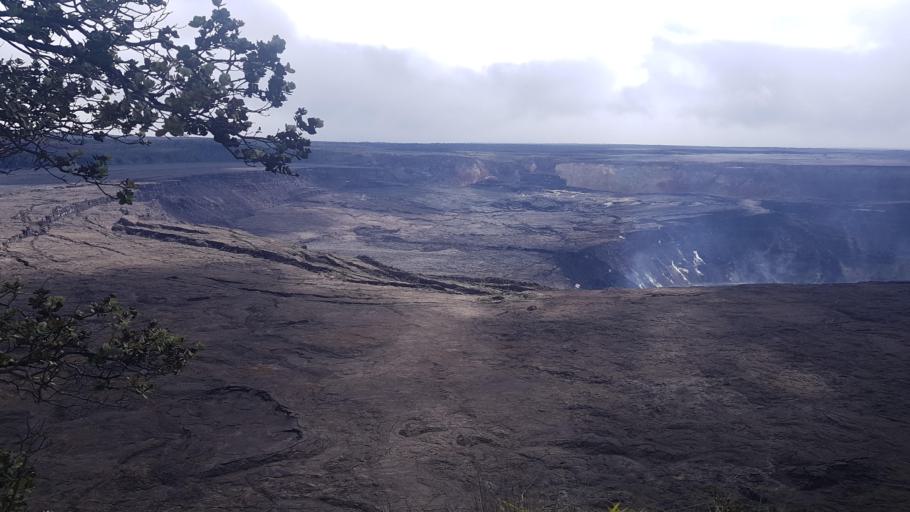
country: US
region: Hawaii
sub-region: Hawaii County
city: Volcano
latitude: 19.4239
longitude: -155.2842
